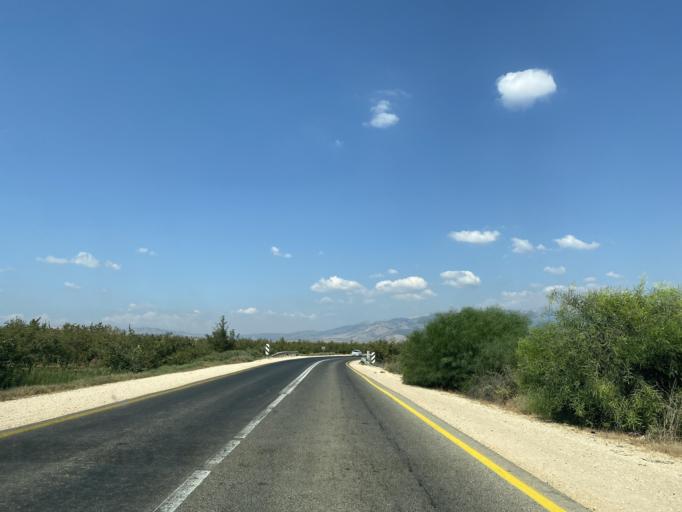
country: IL
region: Northern District
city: Qiryat Shemona
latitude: 33.1707
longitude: 35.5991
